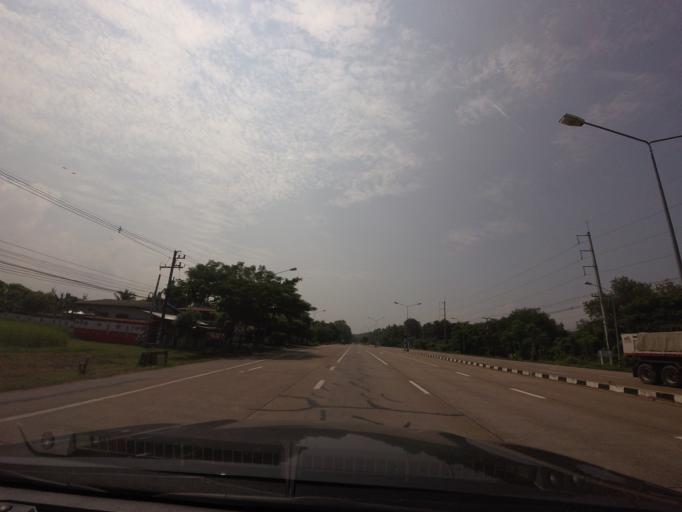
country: TH
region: Phrae
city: Sung Men
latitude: 18.0050
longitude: 100.1044
